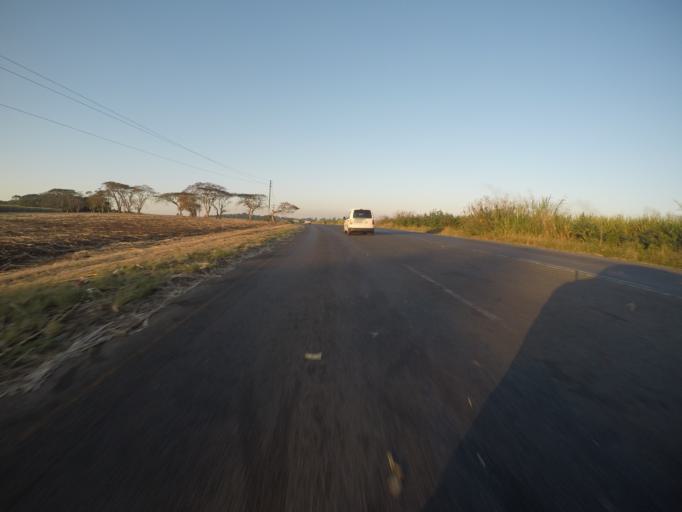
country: ZA
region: KwaZulu-Natal
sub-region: uThungulu District Municipality
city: Empangeni
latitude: -28.7830
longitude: 31.8976
